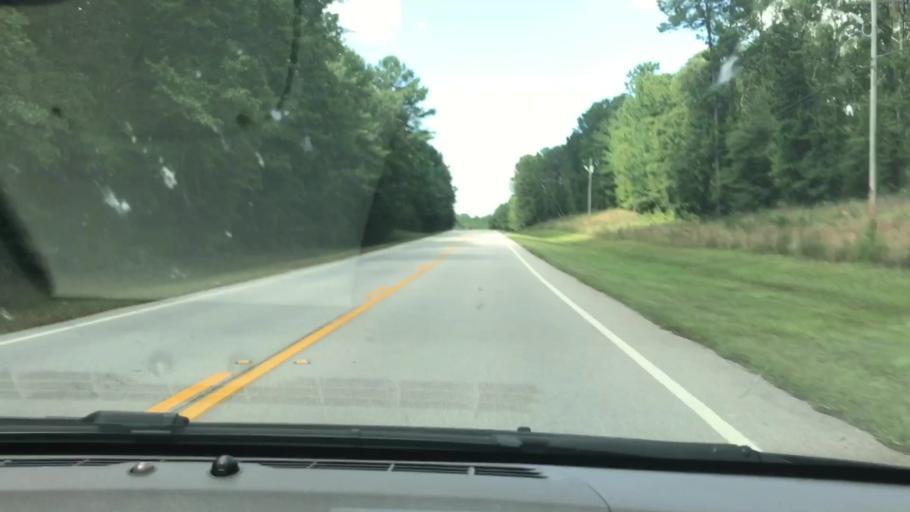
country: US
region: Georgia
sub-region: Troup County
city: La Grange
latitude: 33.0905
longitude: -85.0576
